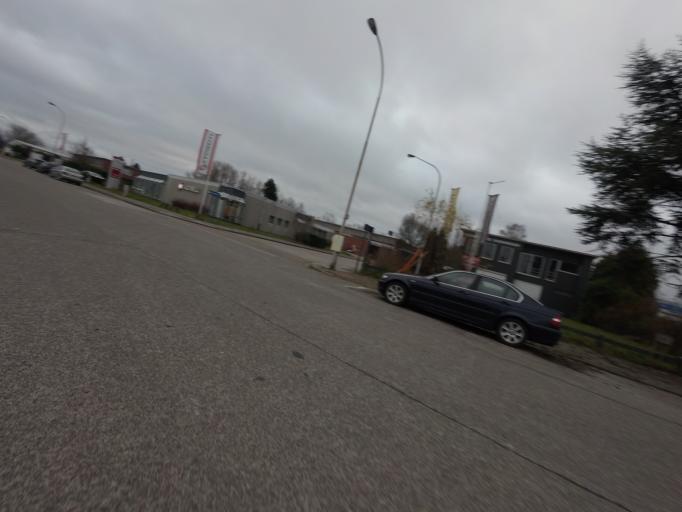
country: BE
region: Flanders
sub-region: Provincie Antwerpen
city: Aartselaar
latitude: 51.1550
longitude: 4.3743
